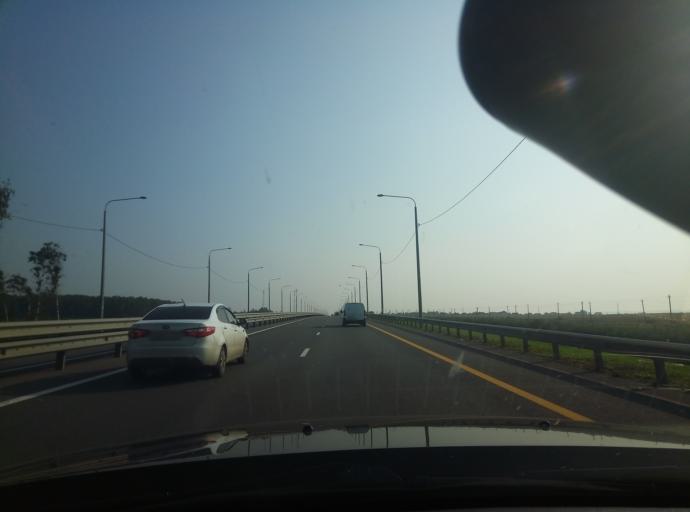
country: RU
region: Kaluga
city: Detchino
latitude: 54.8010
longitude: 36.2768
